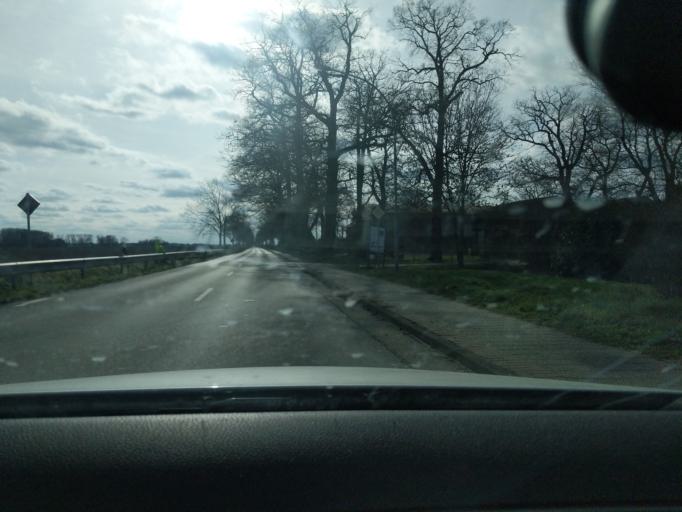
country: DE
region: Lower Saxony
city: Drochtersen
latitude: 53.6943
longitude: 9.4071
